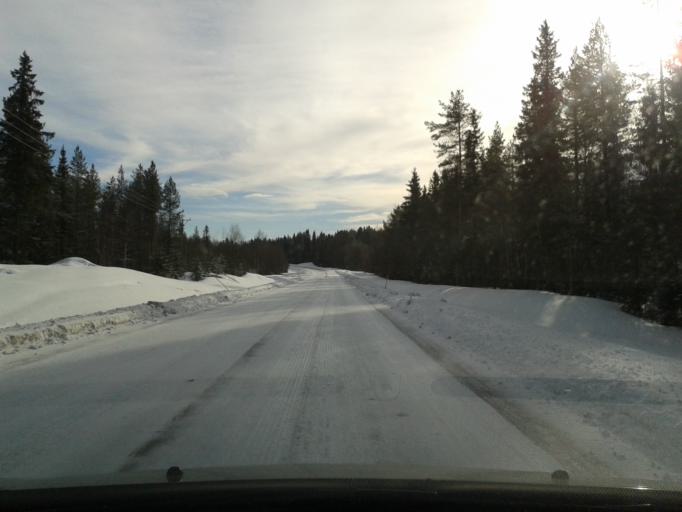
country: SE
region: Vaesterbotten
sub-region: Vilhelmina Kommun
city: Vilhelmina
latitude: 64.5425
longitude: 16.7466
